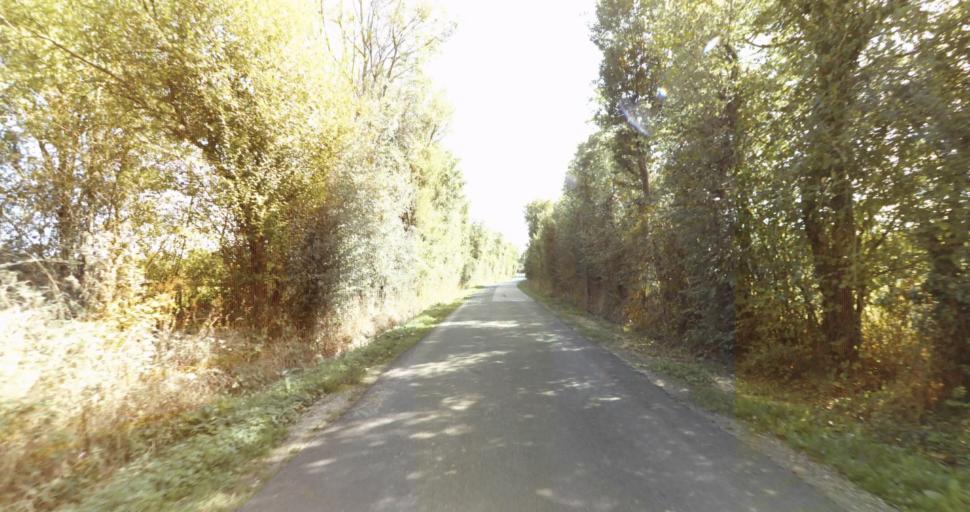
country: FR
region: Lower Normandy
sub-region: Departement de l'Orne
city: Gace
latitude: 48.7271
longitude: 0.2249
